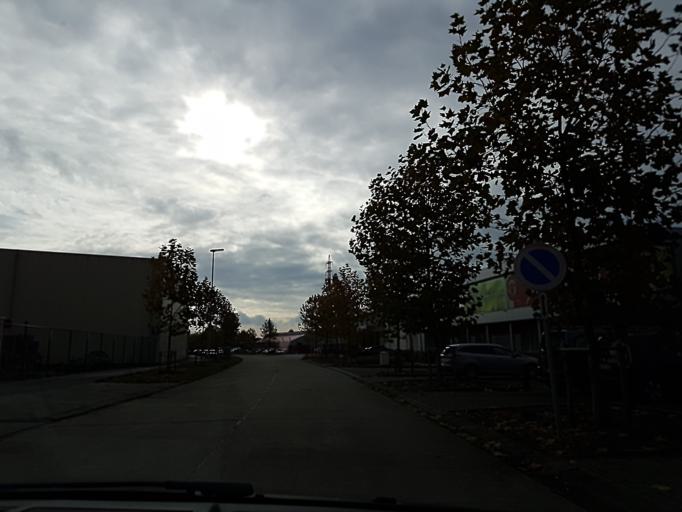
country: BE
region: Flanders
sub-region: Provincie Antwerpen
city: Lier
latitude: 51.1481
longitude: 4.5555
